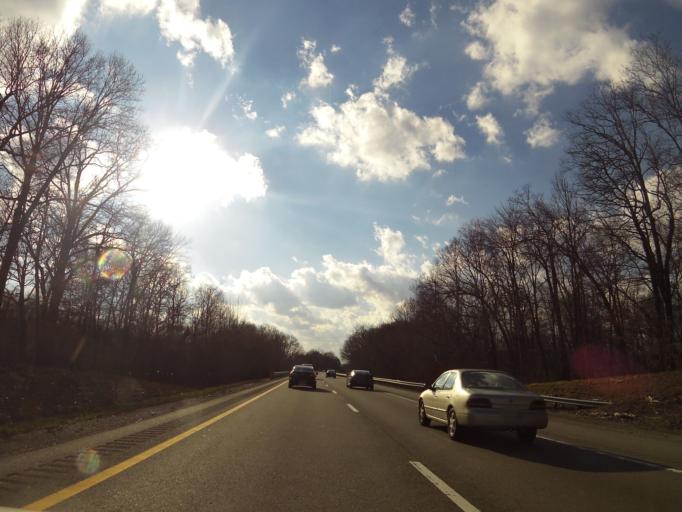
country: US
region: Tennessee
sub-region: Putnam County
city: Cookeville
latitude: 36.1359
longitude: -85.5526
